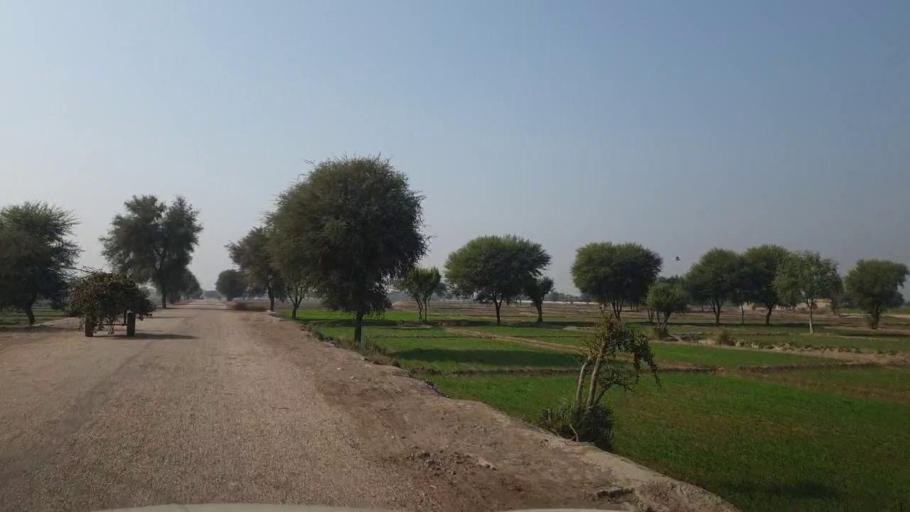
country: PK
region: Sindh
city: Bhan
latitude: 26.5111
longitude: 67.7953
